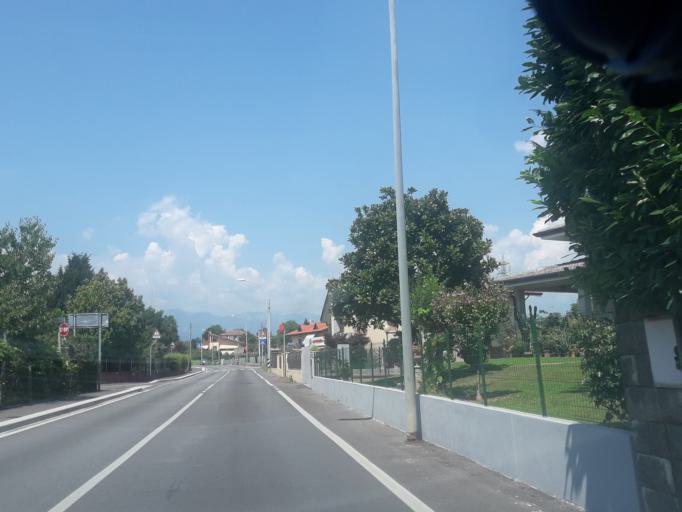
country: IT
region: Friuli Venezia Giulia
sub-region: Provincia di Udine
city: Pagnacco
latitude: 46.1129
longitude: 13.1832
